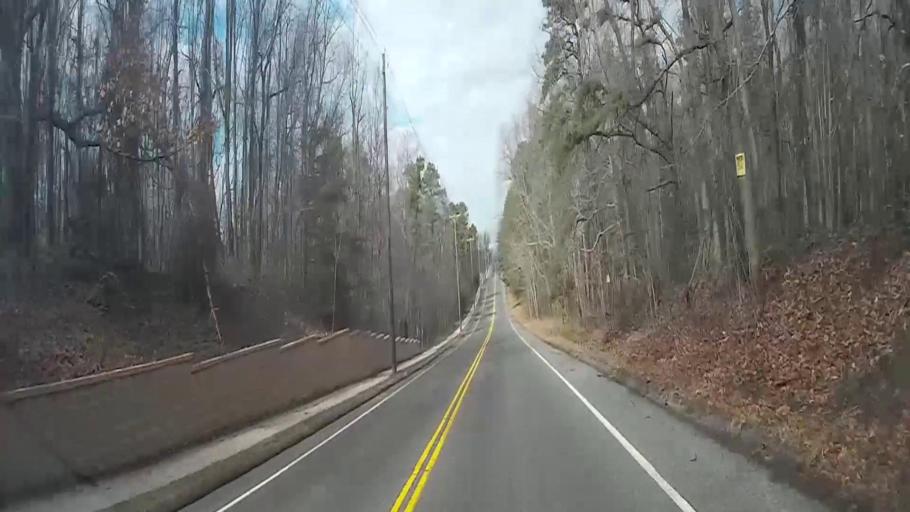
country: US
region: New Jersey
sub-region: Gloucester County
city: Turnersville
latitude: 39.7792
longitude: -75.0337
